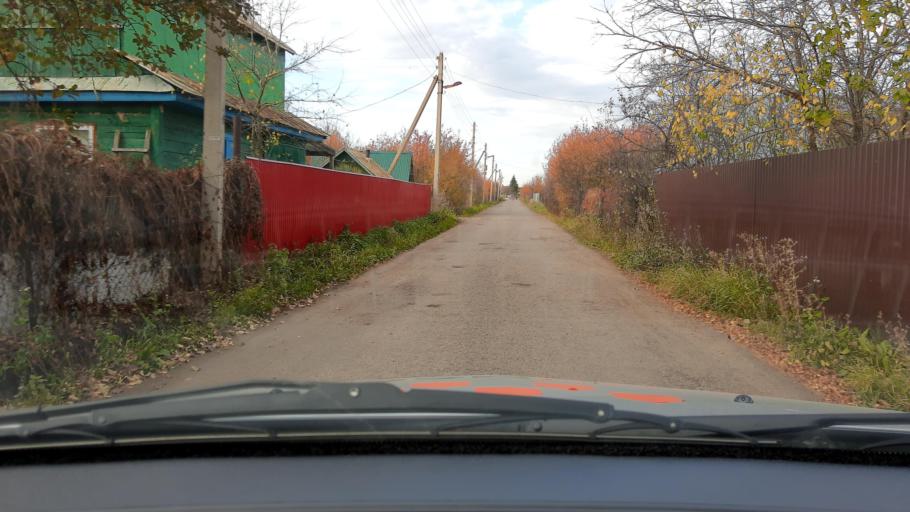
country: RU
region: Bashkortostan
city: Asanovo
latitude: 54.8055
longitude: 55.6051
